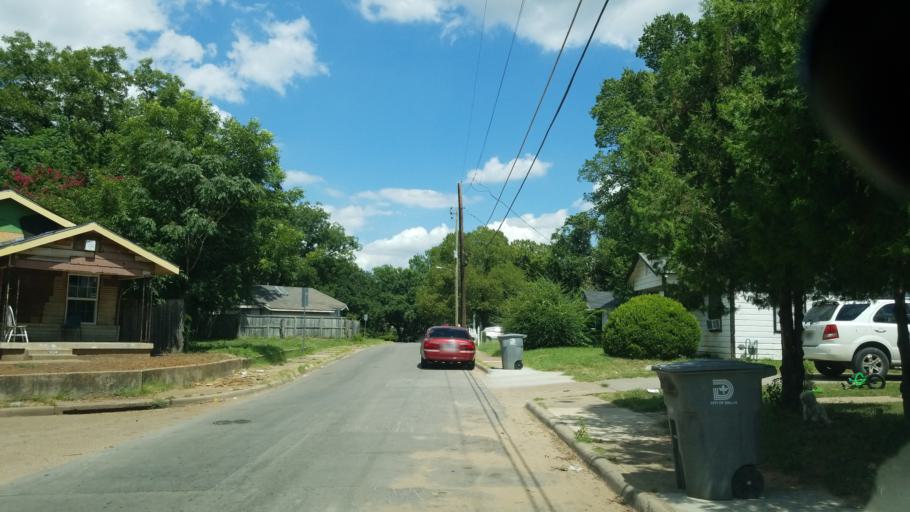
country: US
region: Texas
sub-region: Dallas County
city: Dallas
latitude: 32.7514
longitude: -96.7489
